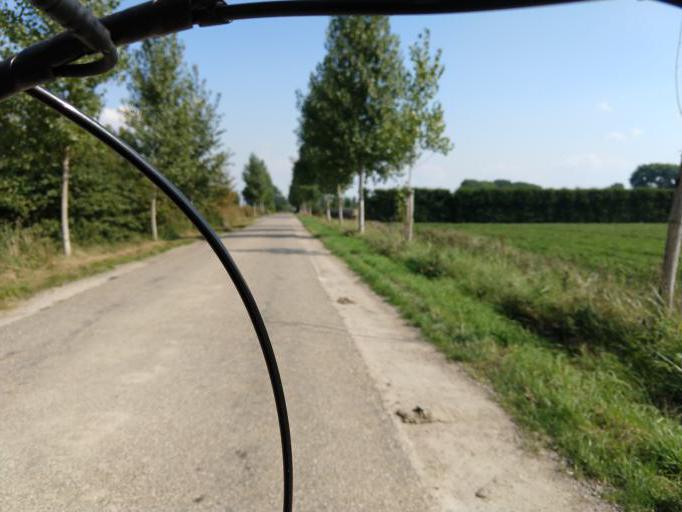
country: NL
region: Zeeland
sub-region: Gemeente Goes
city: Goes
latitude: 51.4405
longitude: 3.8732
